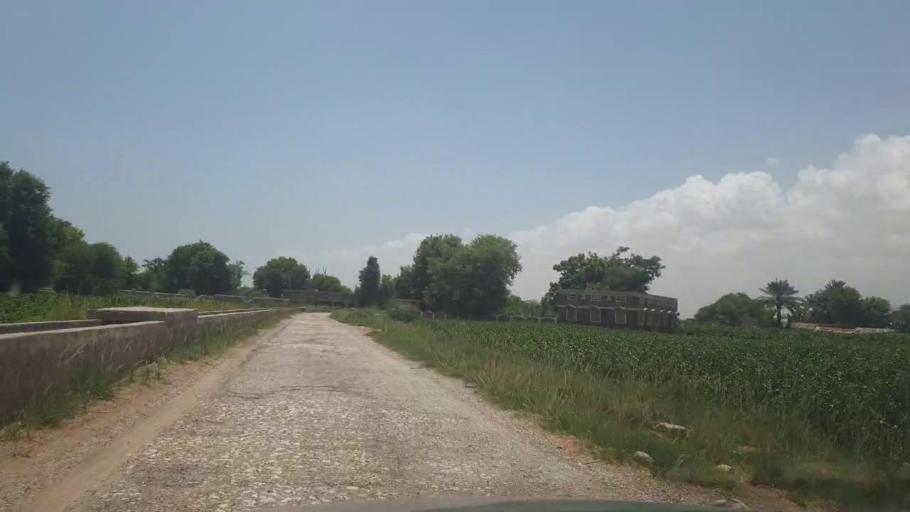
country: PK
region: Sindh
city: Kot Diji
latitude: 27.2658
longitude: 69.0183
